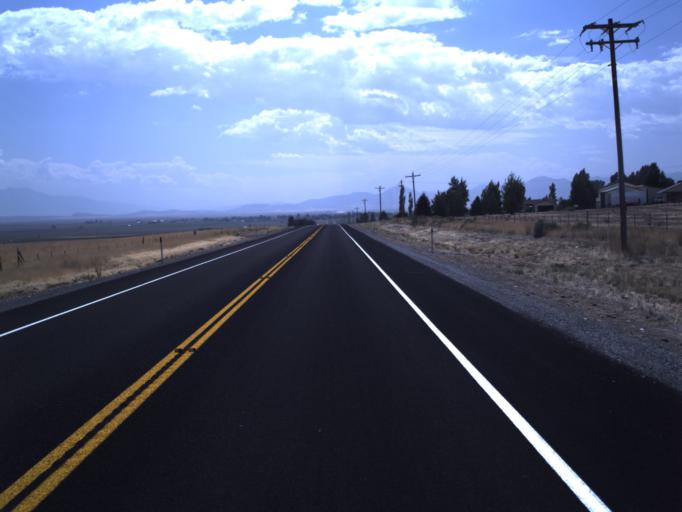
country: US
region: Utah
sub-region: Utah County
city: Eagle Mountain
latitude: 40.3049
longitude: -112.1006
